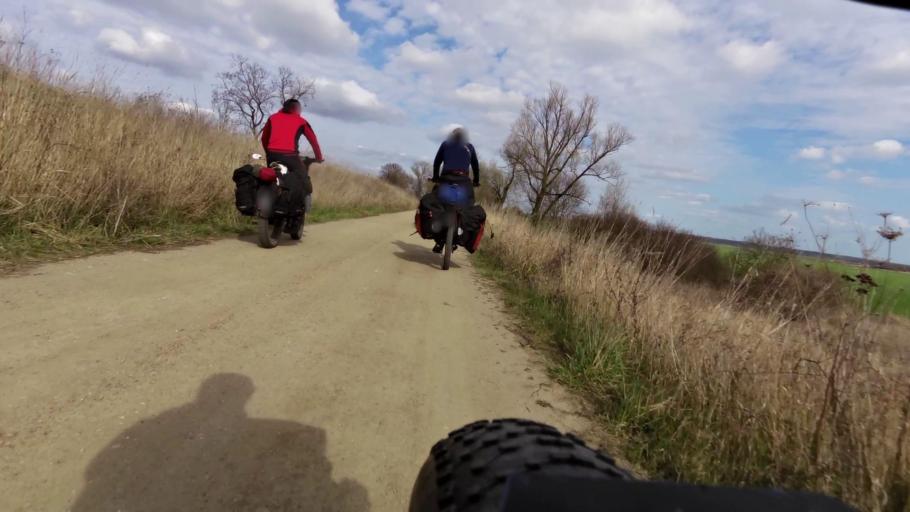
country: DE
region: Brandenburg
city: Lebus
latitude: 52.4375
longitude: 14.5788
